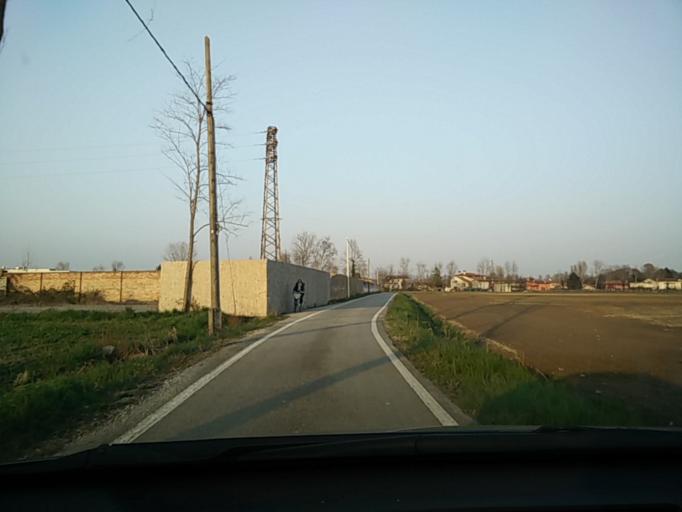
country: IT
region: Veneto
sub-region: Provincia di Venezia
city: Noventa di Piave
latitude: 45.6489
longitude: 12.5386
